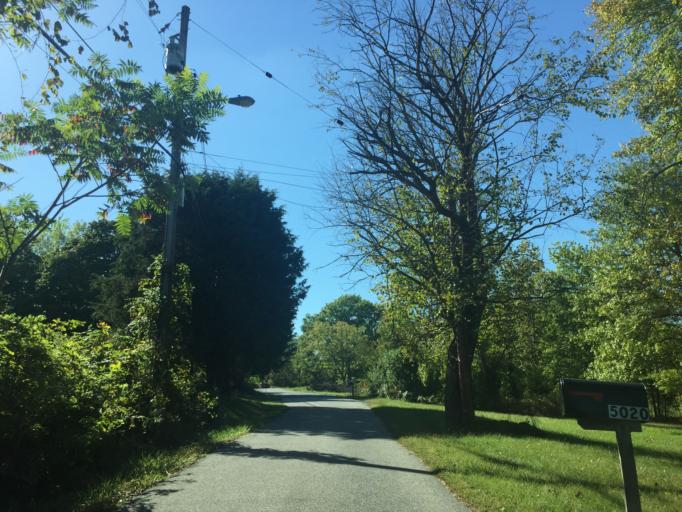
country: US
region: Maryland
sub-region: Baltimore County
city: Perry Hall
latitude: 39.3776
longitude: -76.4803
